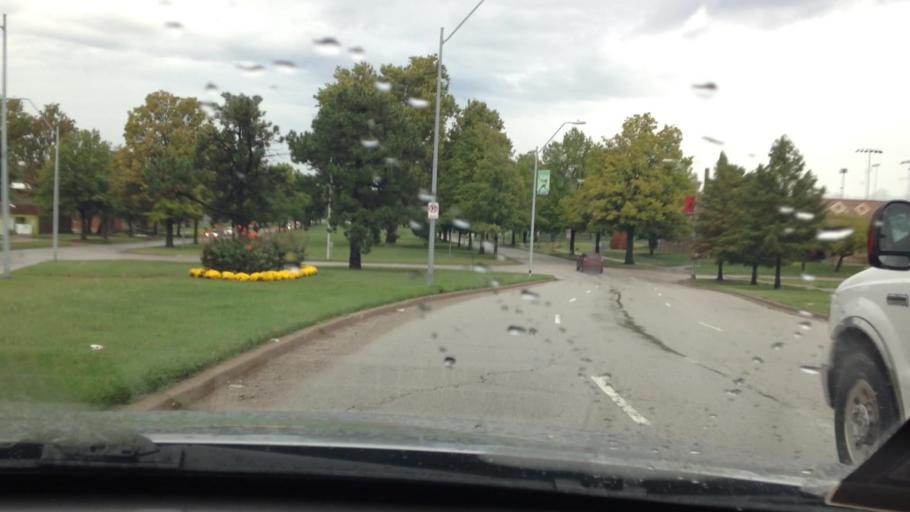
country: US
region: Missouri
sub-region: Jackson County
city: Kansas City
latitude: 39.0913
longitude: -94.5644
